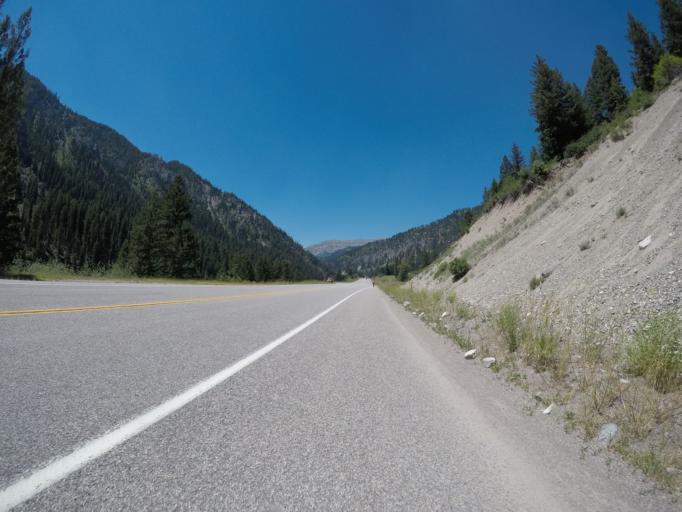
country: US
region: Wyoming
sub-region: Teton County
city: Hoback
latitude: 43.1969
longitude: -110.8882
